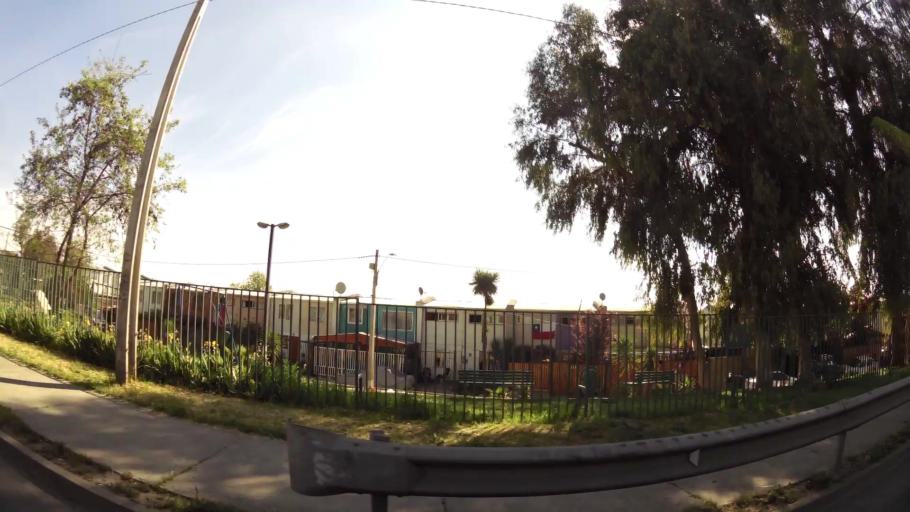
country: CL
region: Santiago Metropolitan
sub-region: Provincia de Santiago
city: Villa Presidente Frei, Nunoa, Santiago, Chile
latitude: -33.4793
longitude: -70.5581
